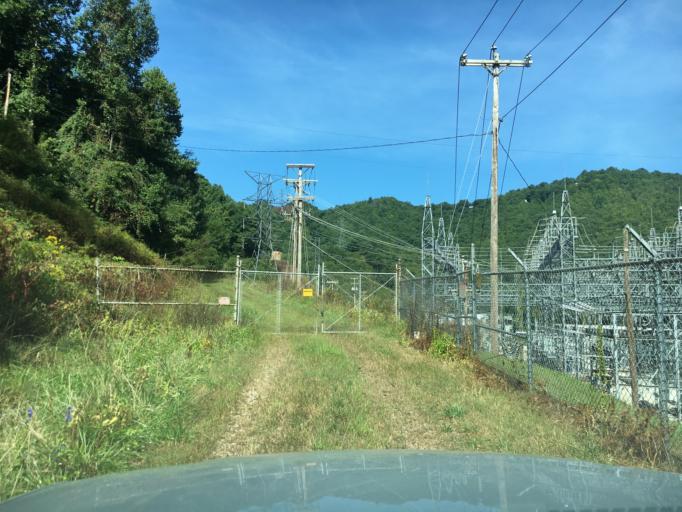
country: US
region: North Carolina
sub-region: Graham County
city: Robbinsville
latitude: 35.2712
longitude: -83.6763
